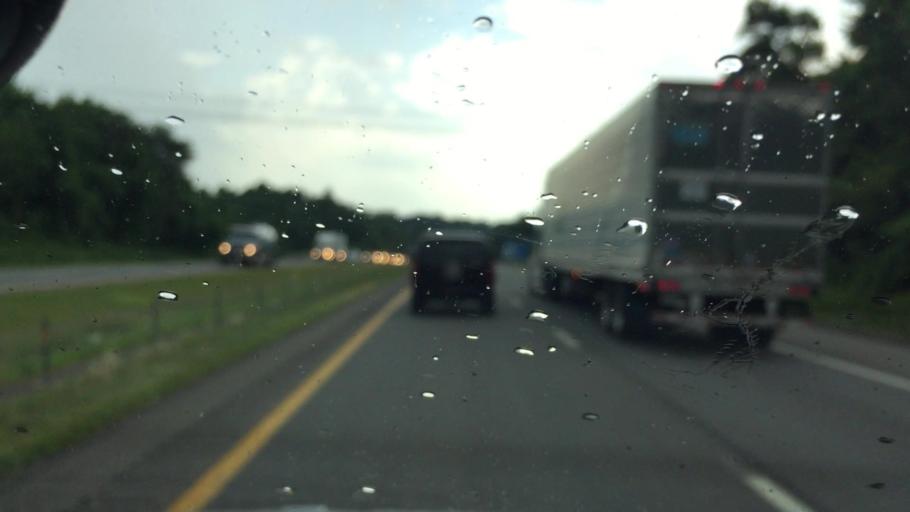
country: US
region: Ohio
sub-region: Belmont County
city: Wolfhurst
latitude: 40.0599
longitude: -80.8305
